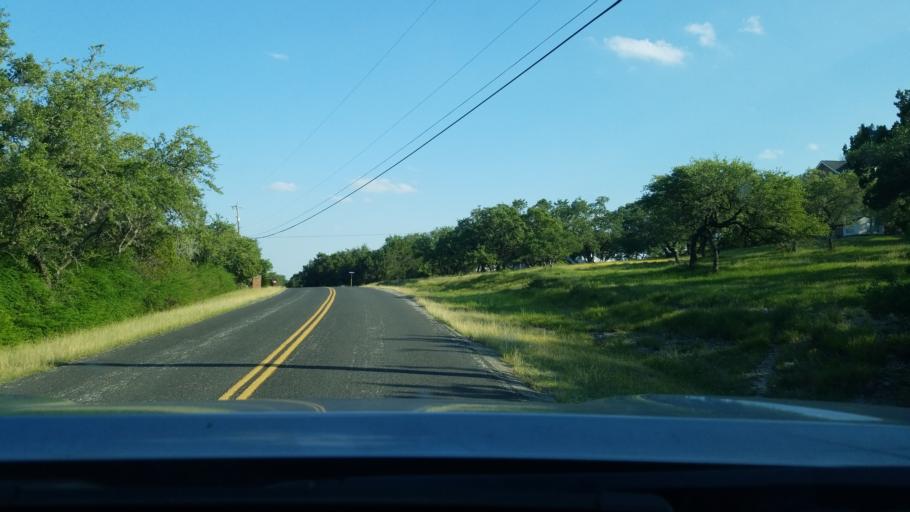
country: US
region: Texas
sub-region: Bexar County
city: Timberwood Park
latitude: 29.7019
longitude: -98.4375
